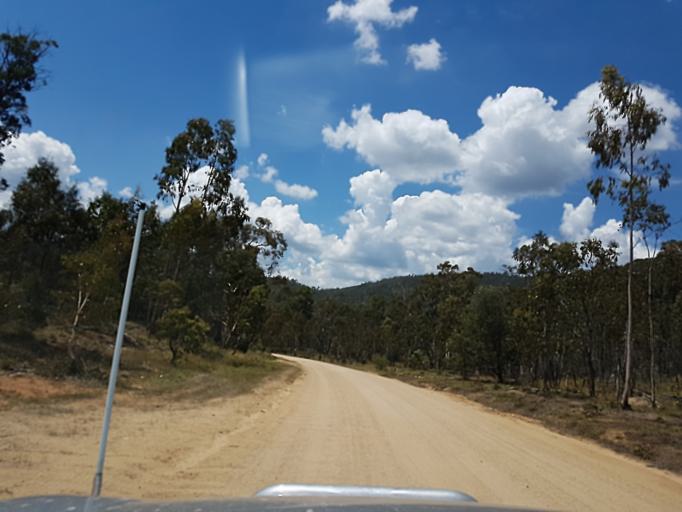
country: AU
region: Victoria
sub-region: Alpine
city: Mount Beauty
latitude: -36.9001
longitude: 147.8265
